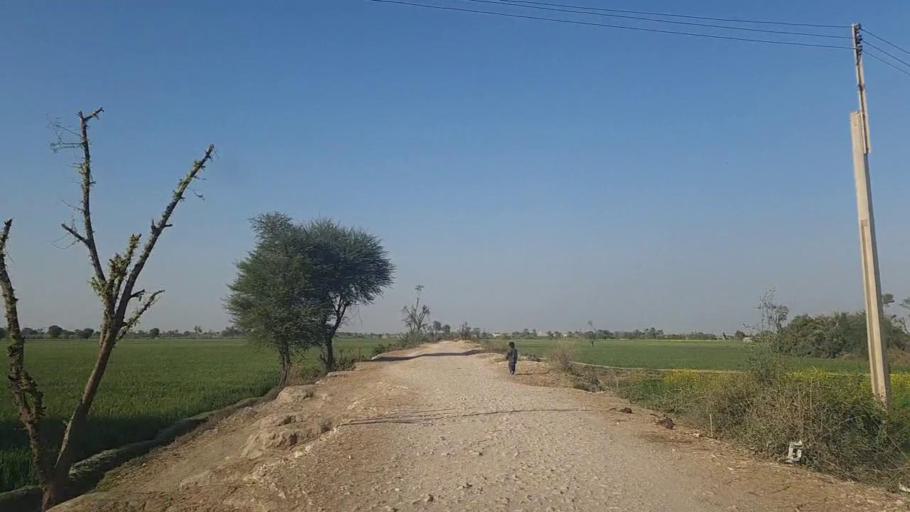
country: PK
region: Sindh
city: Jam Sahib
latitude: 26.3132
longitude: 68.7150
